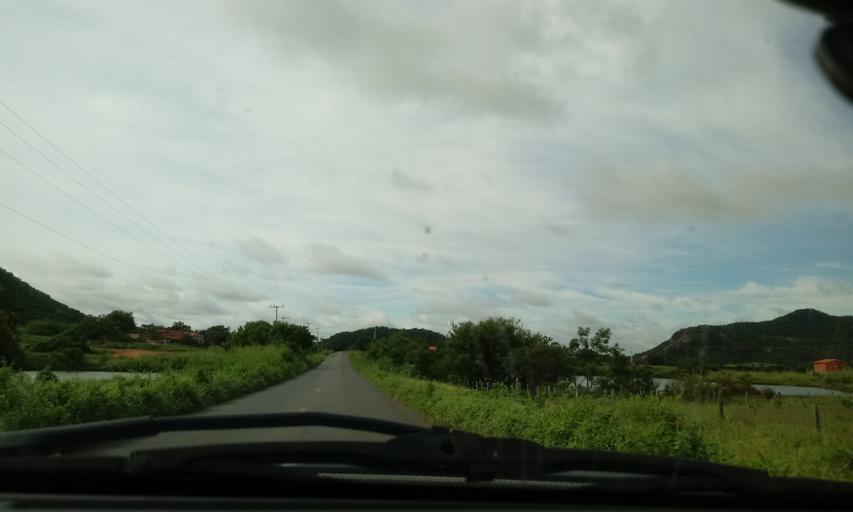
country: BR
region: Bahia
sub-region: Guanambi
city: Guanambi
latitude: -14.1274
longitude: -42.8527
